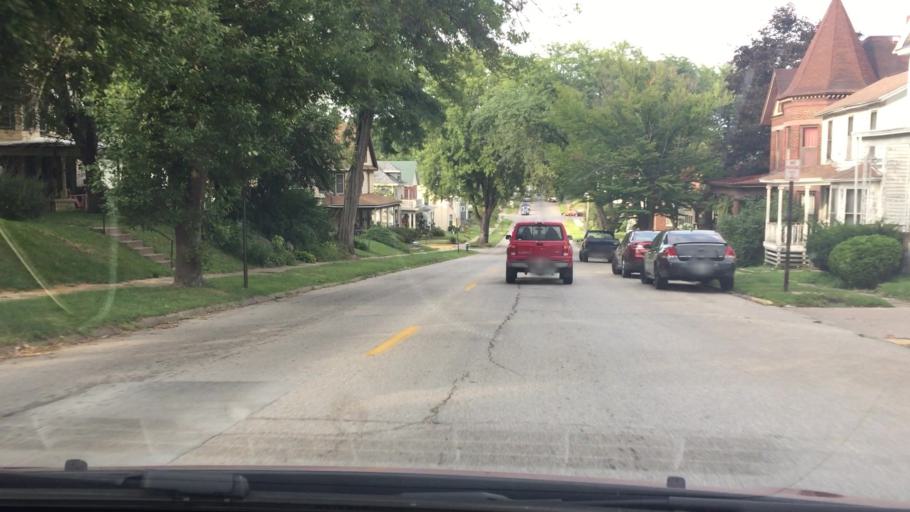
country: US
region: Iowa
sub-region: Muscatine County
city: Muscatine
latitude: 41.4262
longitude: -91.0502
